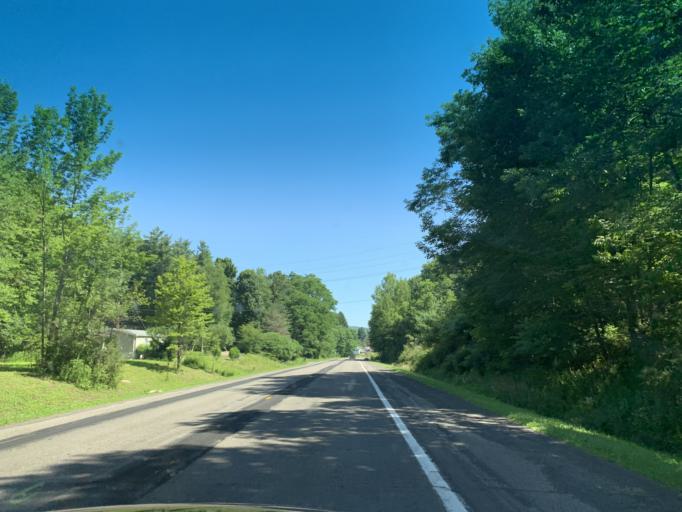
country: US
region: New York
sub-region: Delaware County
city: Sidney
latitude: 42.3976
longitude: -75.3962
